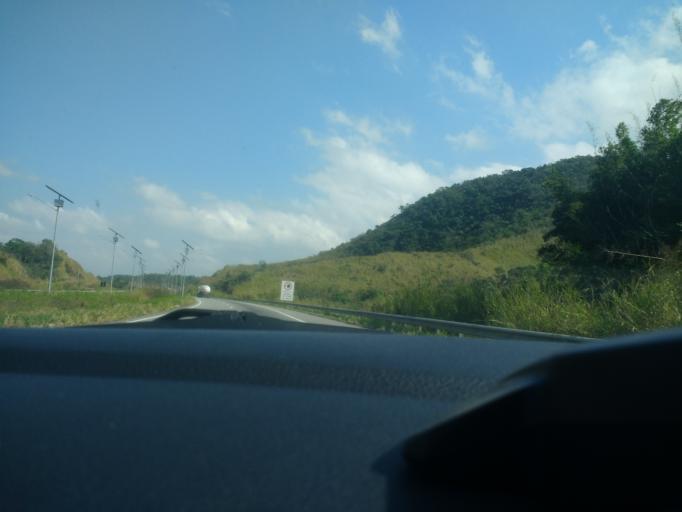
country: BR
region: Rio de Janeiro
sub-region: Queimados
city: Queimados
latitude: -22.6871
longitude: -43.4896
